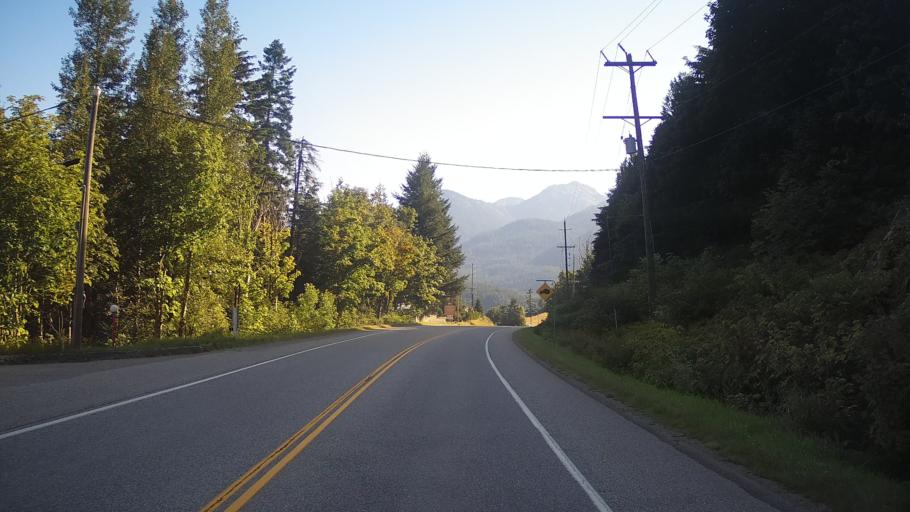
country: CA
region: British Columbia
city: Hope
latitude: 49.4126
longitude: -121.4413
